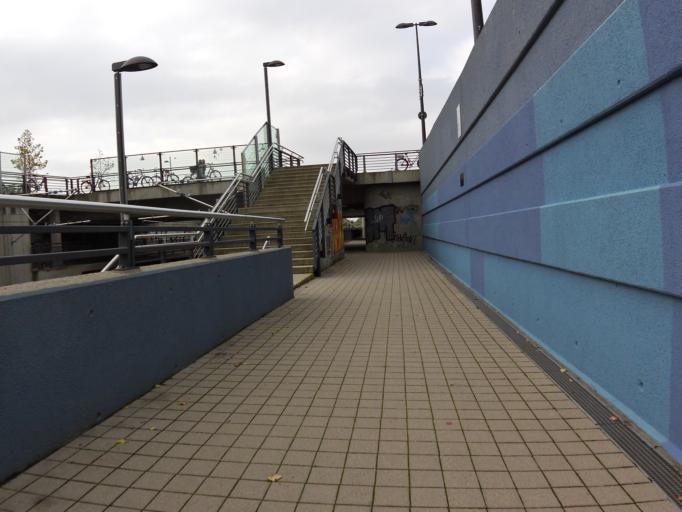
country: DE
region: Saxony
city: Leipzig
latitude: 51.3203
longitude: 12.3863
